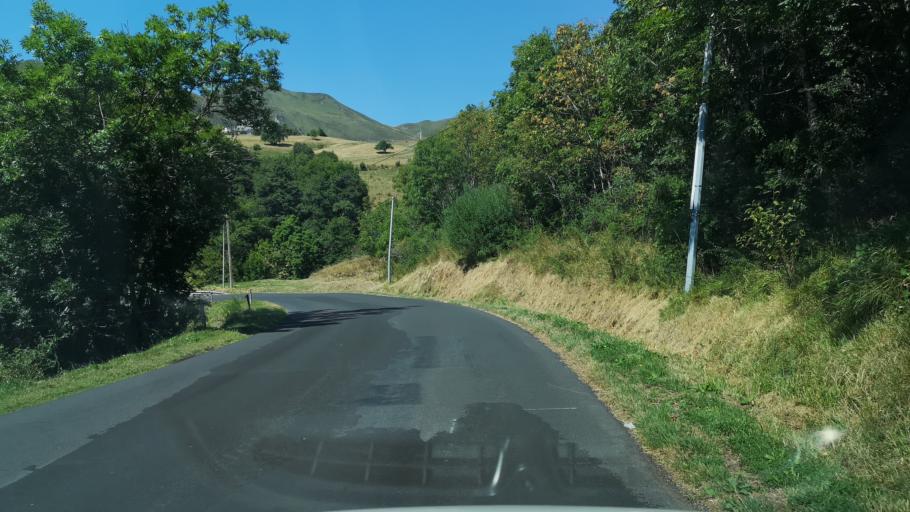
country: FR
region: Auvergne
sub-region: Departement du Puy-de-Dome
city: Mont-Dore
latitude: 45.5781
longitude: 2.8818
